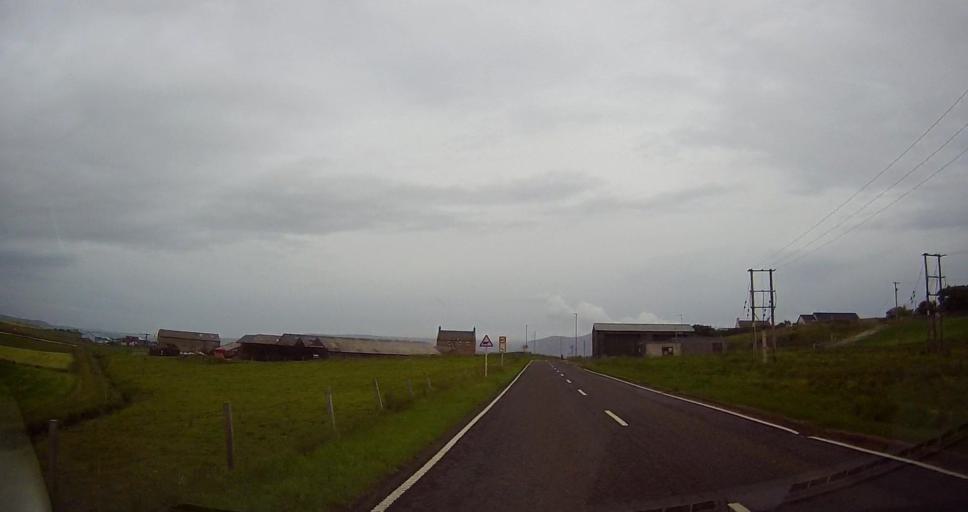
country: GB
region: Scotland
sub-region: Orkney Islands
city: Stromness
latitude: 58.9754
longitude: -3.2880
